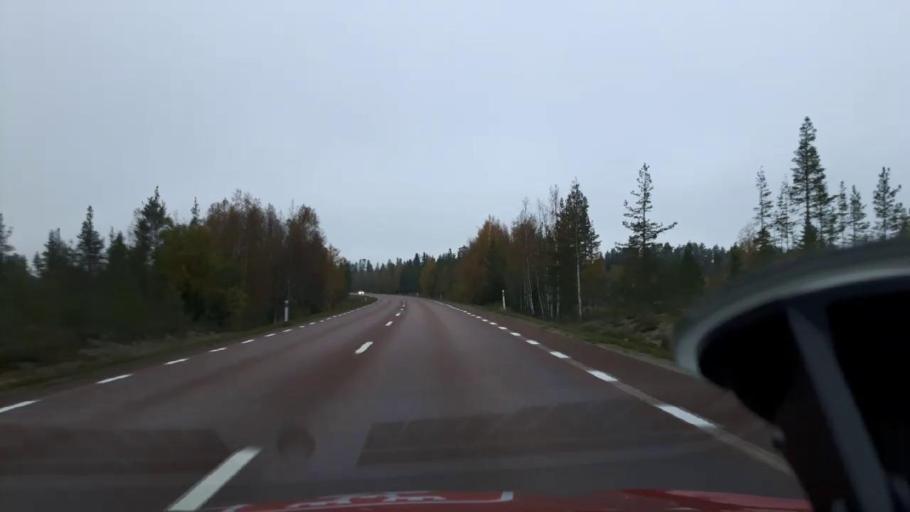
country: SE
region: Jaemtland
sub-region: Bergs Kommun
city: Hoverberg
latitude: 62.5105
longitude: 14.4497
